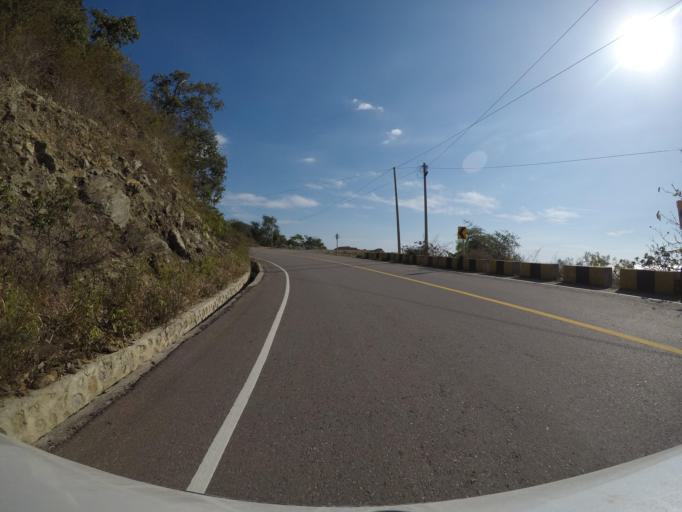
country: TL
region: Liquica
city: Maubara
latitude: -8.6466
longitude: 125.1231
